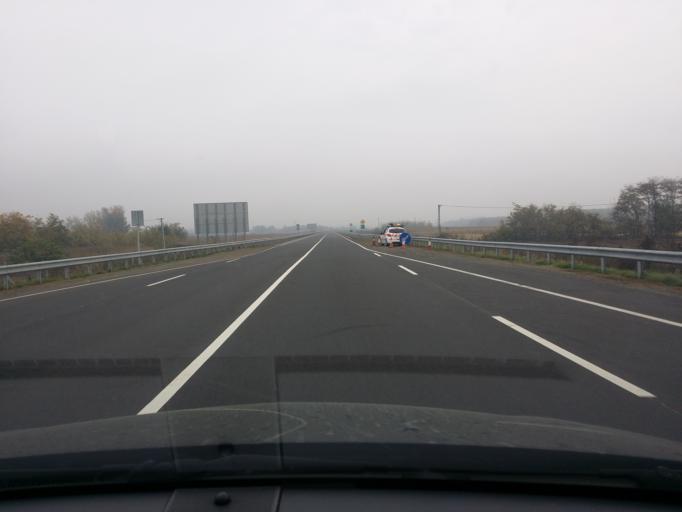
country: HU
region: Szabolcs-Szatmar-Bereg
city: Kalmanhaza
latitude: 47.9060
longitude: 21.6432
